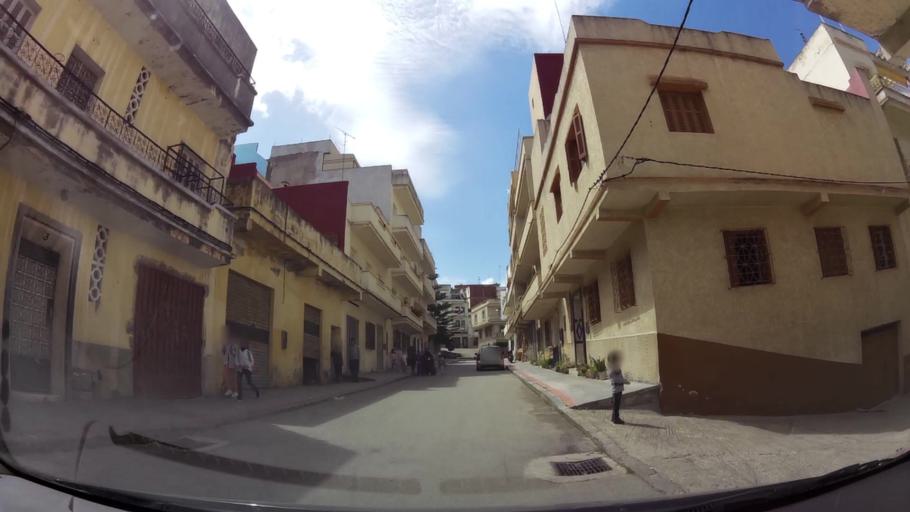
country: MA
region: Tanger-Tetouan
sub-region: Tanger-Assilah
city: Tangier
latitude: 35.7605
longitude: -5.8153
